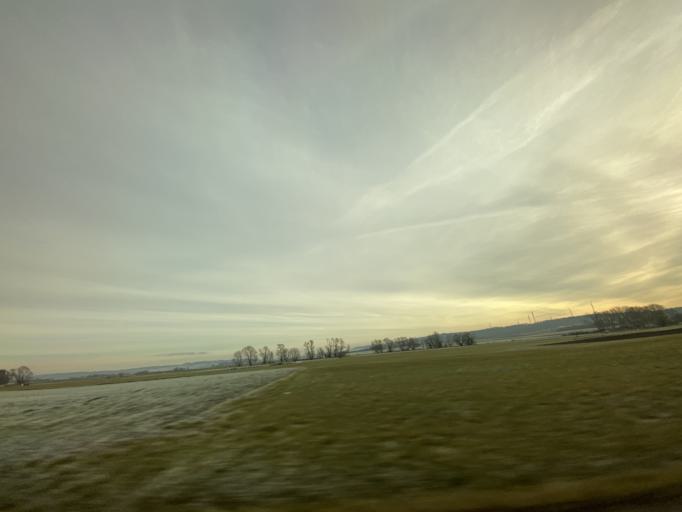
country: DE
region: Hesse
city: Amoneburg
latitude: 50.7807
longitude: 8.9035
